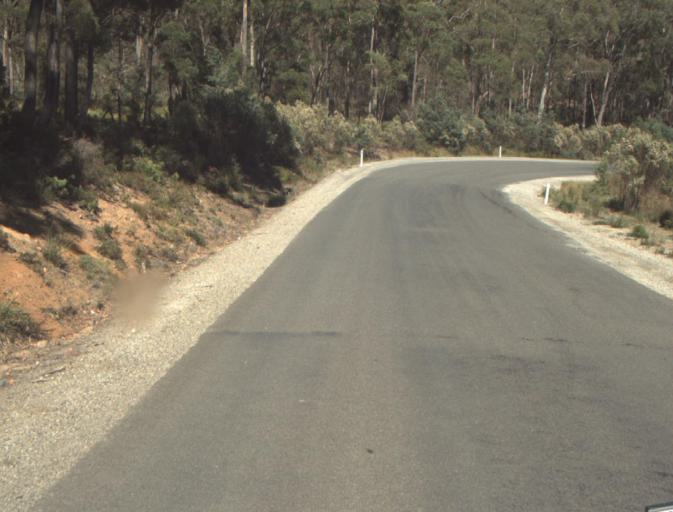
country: AU
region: Tasmania
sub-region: Launceston
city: Mayfield
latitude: -41.3364
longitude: 147.1970
